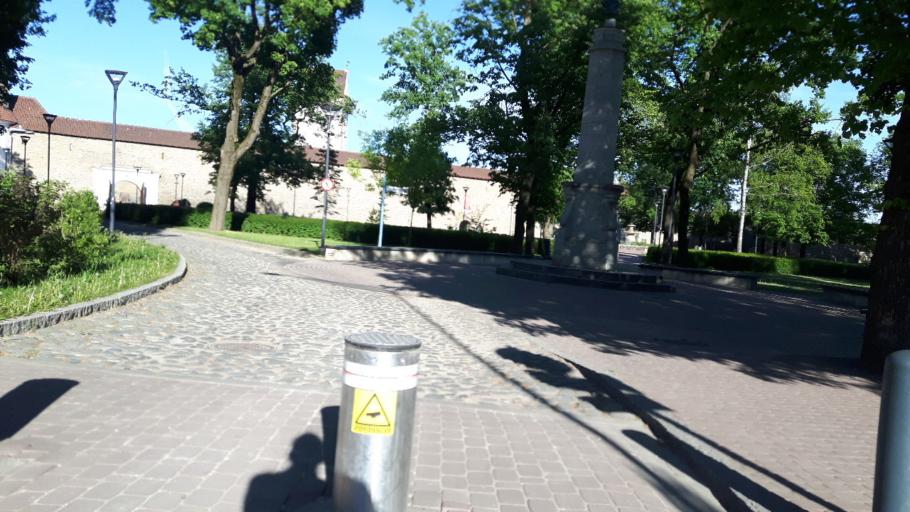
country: EE
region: Ida-Virumaa
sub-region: Narva linn
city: Narva
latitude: 59.3760
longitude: 28.1966
